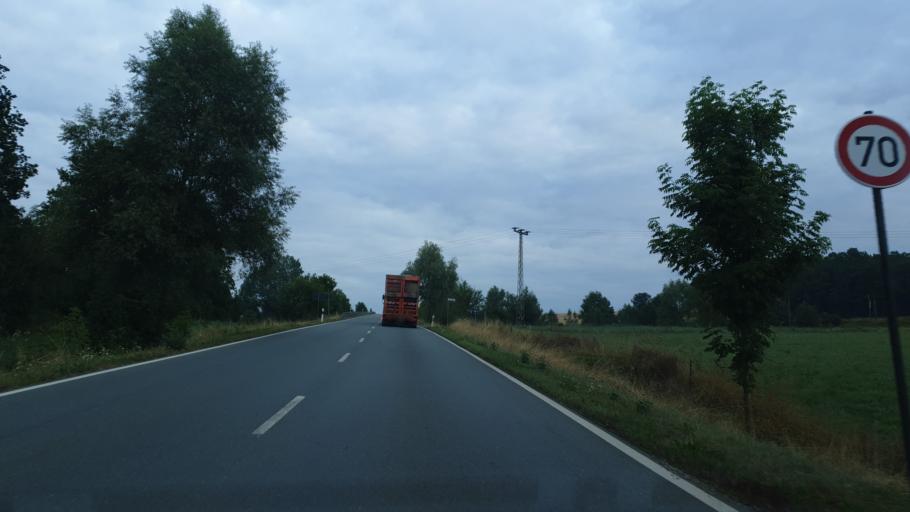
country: DE
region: Saxony
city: Sankt Egidien
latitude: 50.7862
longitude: 12.6325
